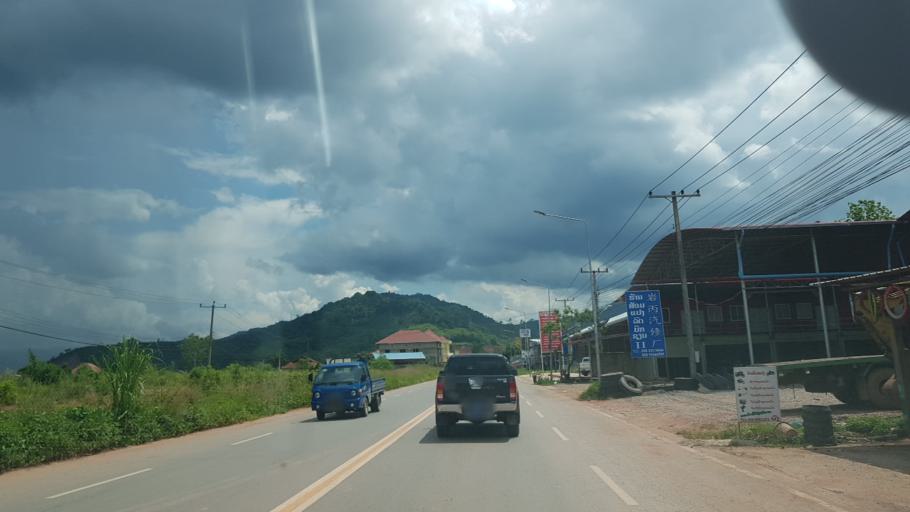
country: LA
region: Oudomxai
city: Muang Xay
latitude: 20.6676
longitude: 101.9818
